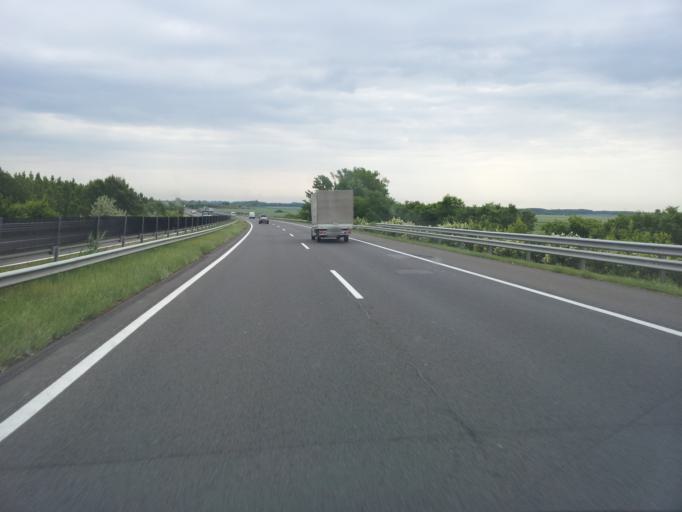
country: HU
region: Heves
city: Karacsond
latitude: 47.7072
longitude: 20.0159
